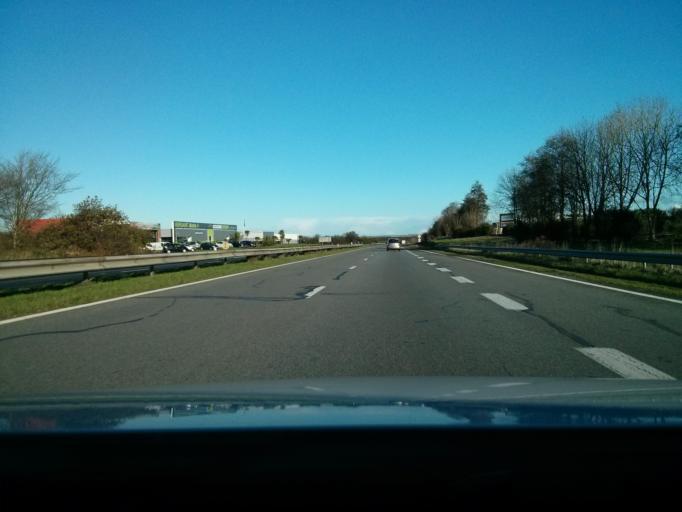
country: FR
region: Brittany
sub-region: Departement du Finistere
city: Kersaint-Plabennec
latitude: 48.4597
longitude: -4.3595
